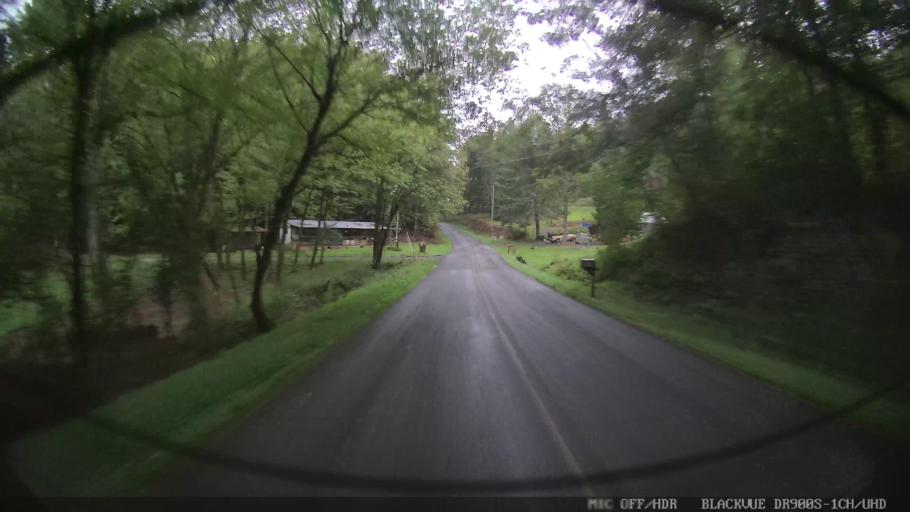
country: US
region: Georgia
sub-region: Gilmer County
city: Ellijay
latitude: 34.7789
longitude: -84.5430
